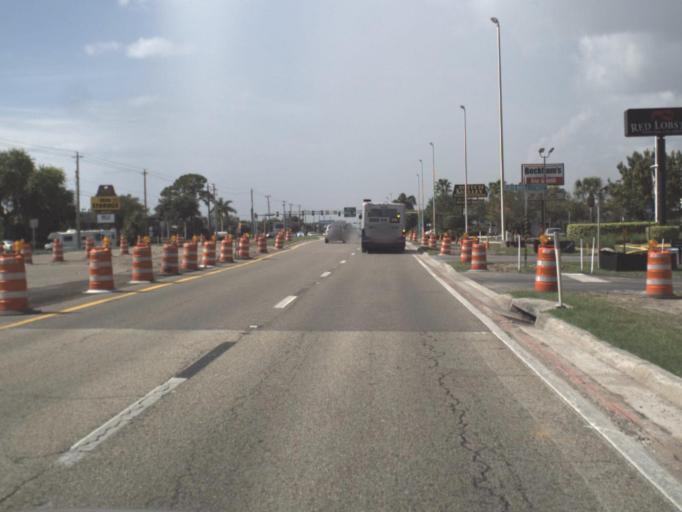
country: US
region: Florida
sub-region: Sarasota County
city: Gulf Gate Estates
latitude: 27.2568
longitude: -82.5190
